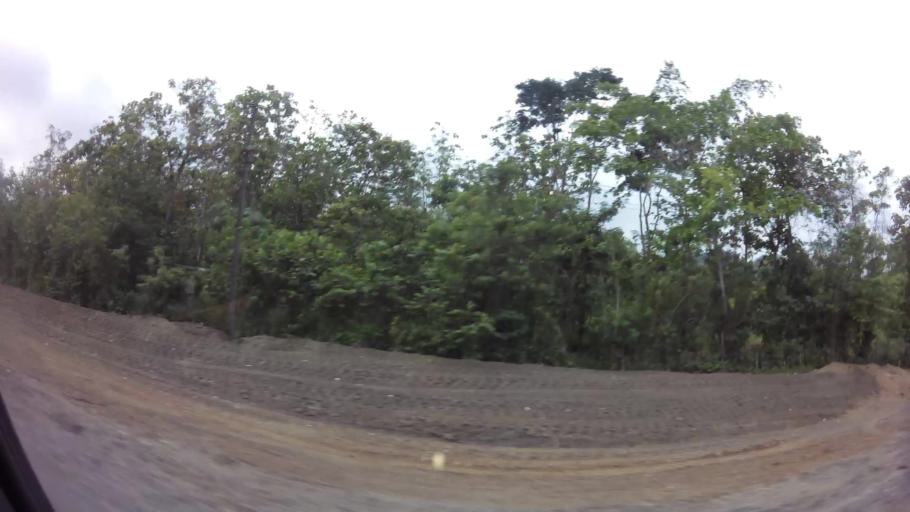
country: HN
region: Yoro
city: Guaimitas
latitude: 15.4953
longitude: -87.7213
